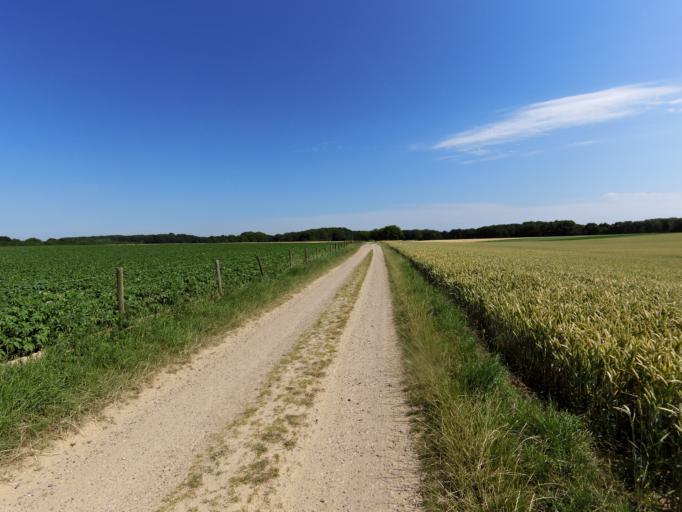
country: NL
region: Limburg
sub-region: Valkenburg aan de Geul
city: Sibbe
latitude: 50.8409
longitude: 5.8423
